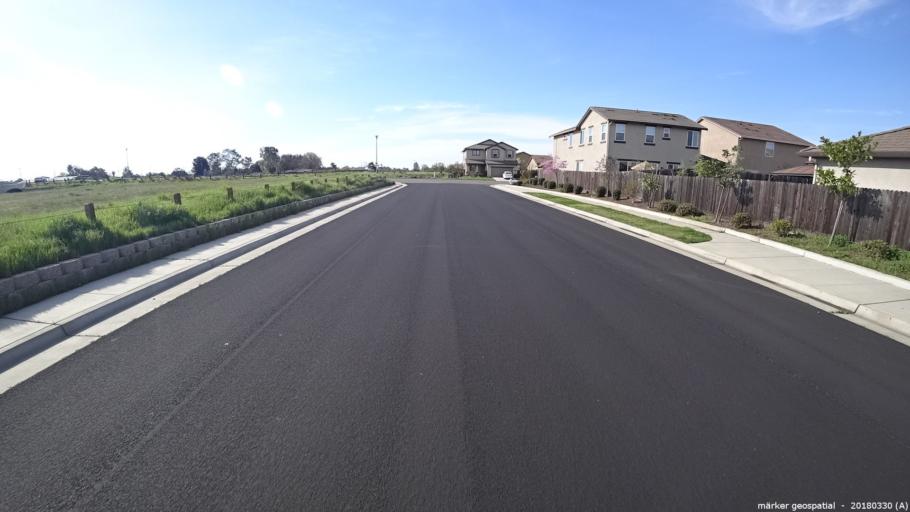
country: US
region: California
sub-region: Sacramento County
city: Vineyard
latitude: 38.4858
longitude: -121.3395
